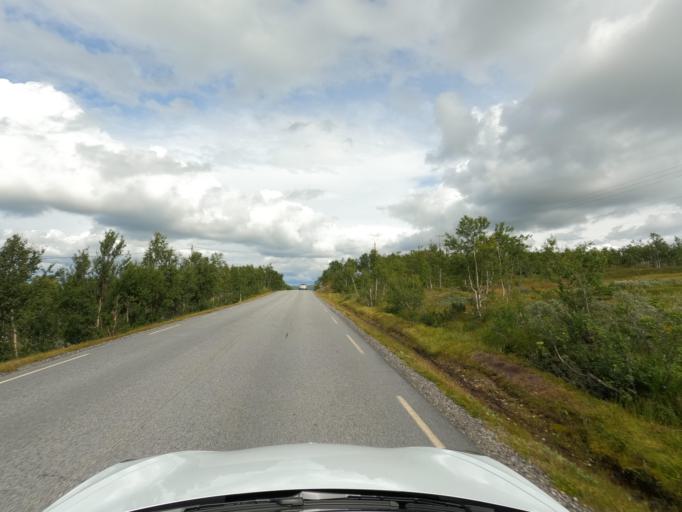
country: NO
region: Telemark
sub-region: Vinje
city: Amot
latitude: 59.7925
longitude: 8.2473
